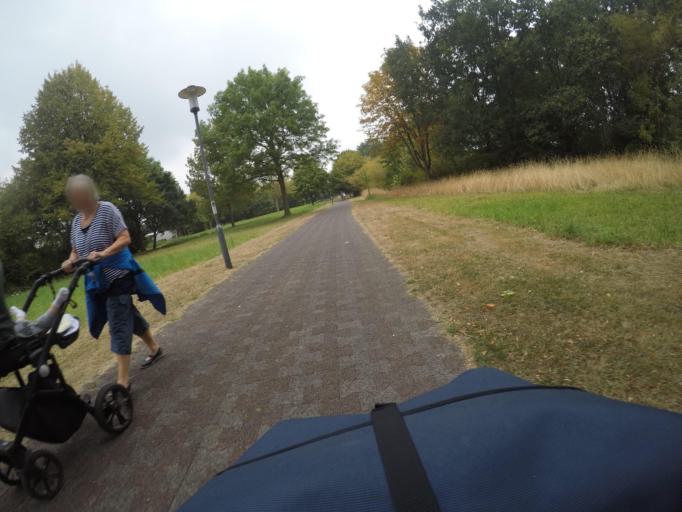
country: DE
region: North Rhine-Westphalia
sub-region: Regierungsbezirk Dusseldorf
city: Krefeld
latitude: 51.3100
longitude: 6.5934
